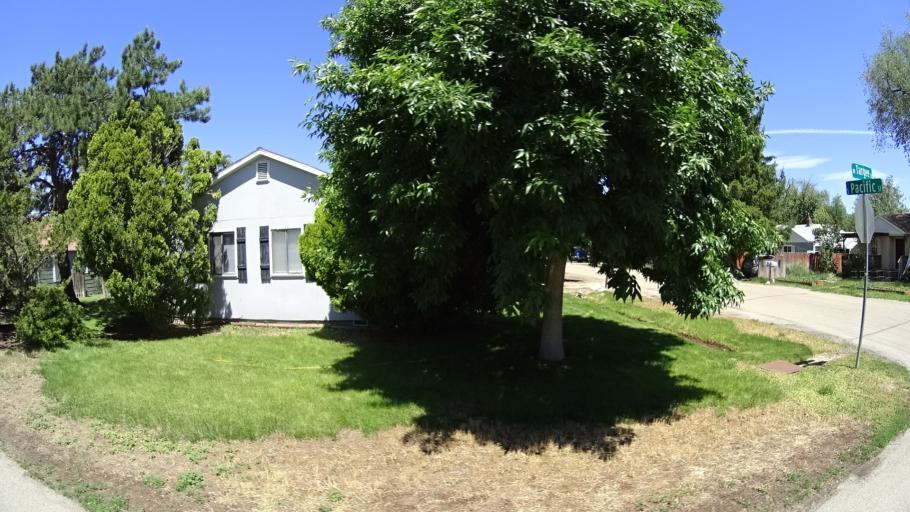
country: US
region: Idaho
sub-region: Ada County
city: Boise
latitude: 43.5825
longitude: -116.2274
